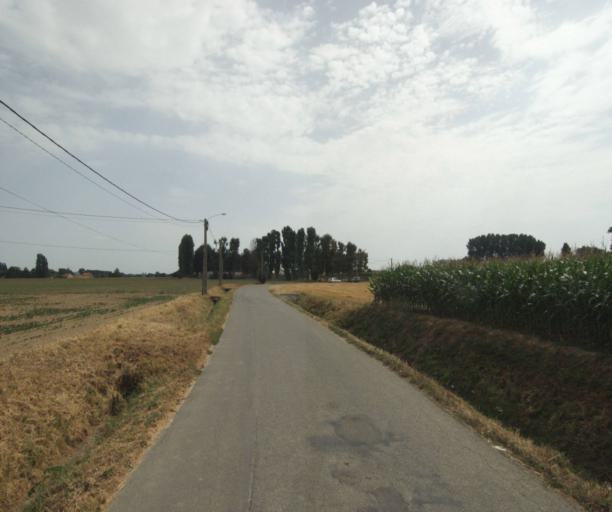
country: BE
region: Wallonia
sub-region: Province du Hainaut
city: Estaimpuis
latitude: 50.7035
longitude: 3.2502
